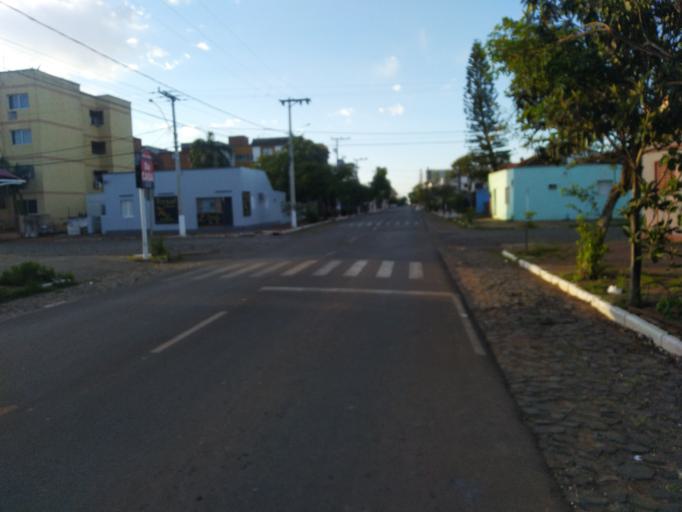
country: BR
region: Rio Grande do Sul
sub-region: Sao Borja
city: Sao Borja
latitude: -28.6555
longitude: -56.0100
